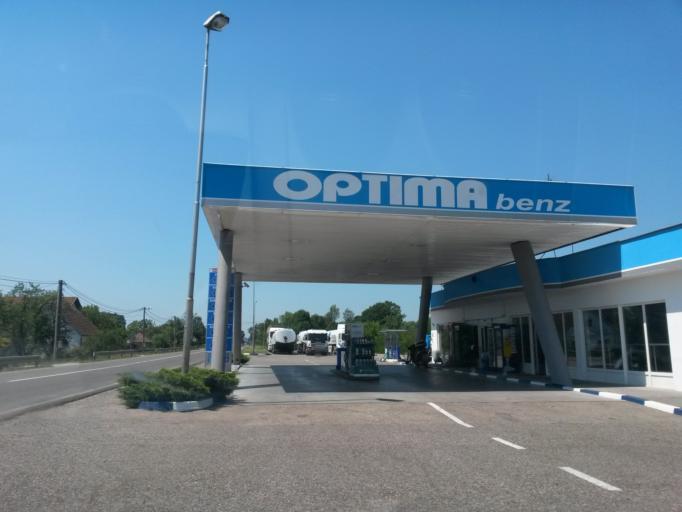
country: BA
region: Federation of Bosnia and Herzegovina
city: Donja Dubica
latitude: 45.0298
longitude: 18.4275
